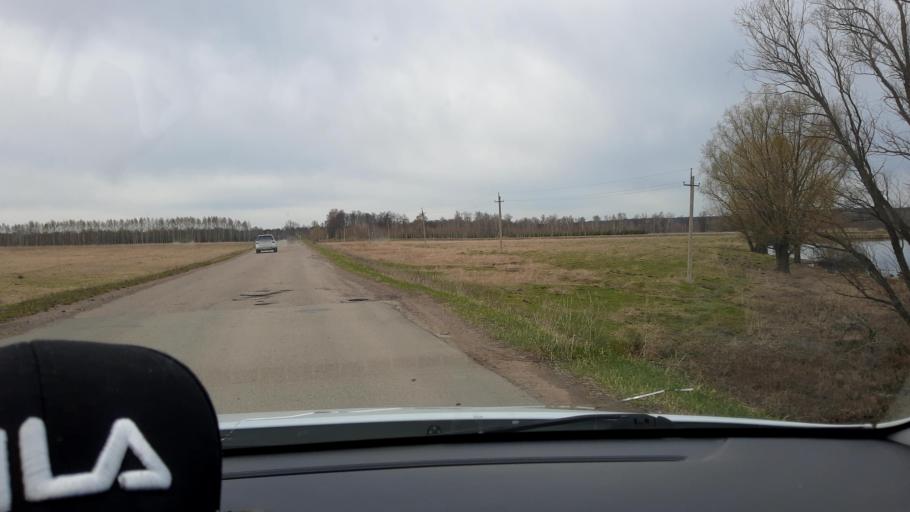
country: RU
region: Bashkortostan
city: Iglino
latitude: 54.7799
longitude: 56.5377
